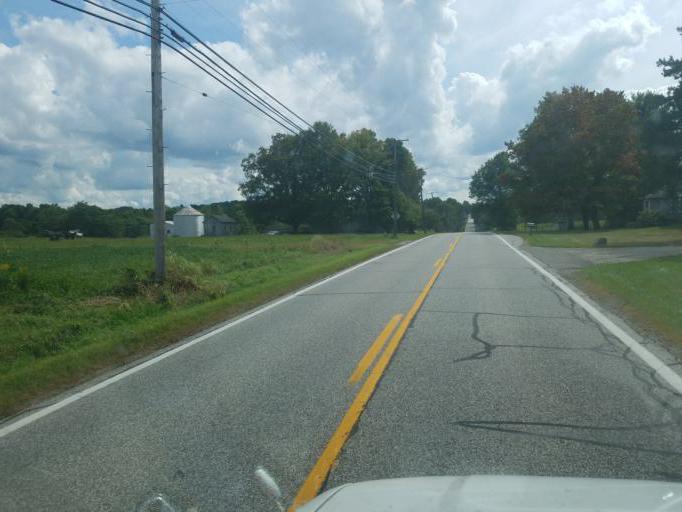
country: US
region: Ohio
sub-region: Geauga County
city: Burton
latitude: 41.3977
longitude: -81.1443
